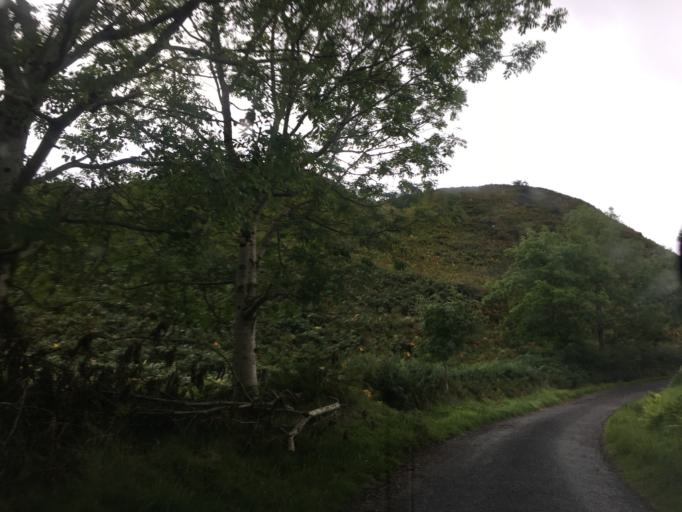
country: GB
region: Scotland
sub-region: Argyll and Bute
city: Oban
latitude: 56.2612
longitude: -5.4690
